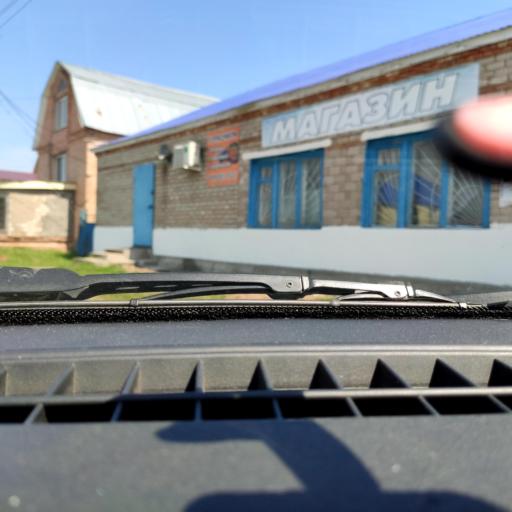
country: RU
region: Bashkortostan
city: Kabakovo
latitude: 54.4633
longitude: 55.9568
